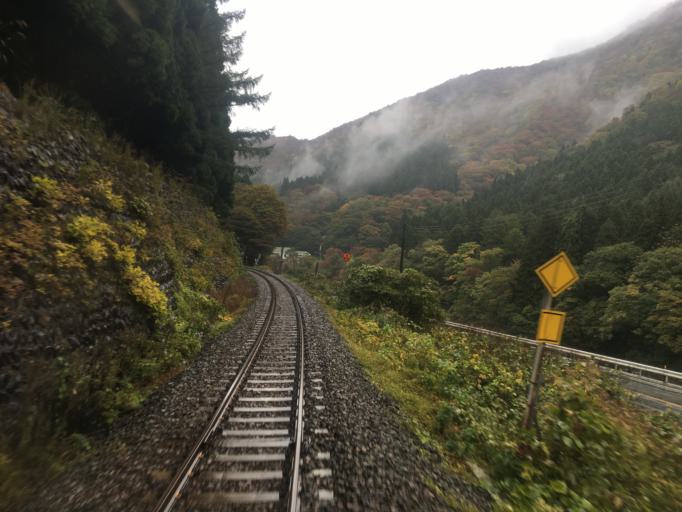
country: JP
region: Yamagata
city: Shinjo
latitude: 38.7556
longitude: 140.4255
